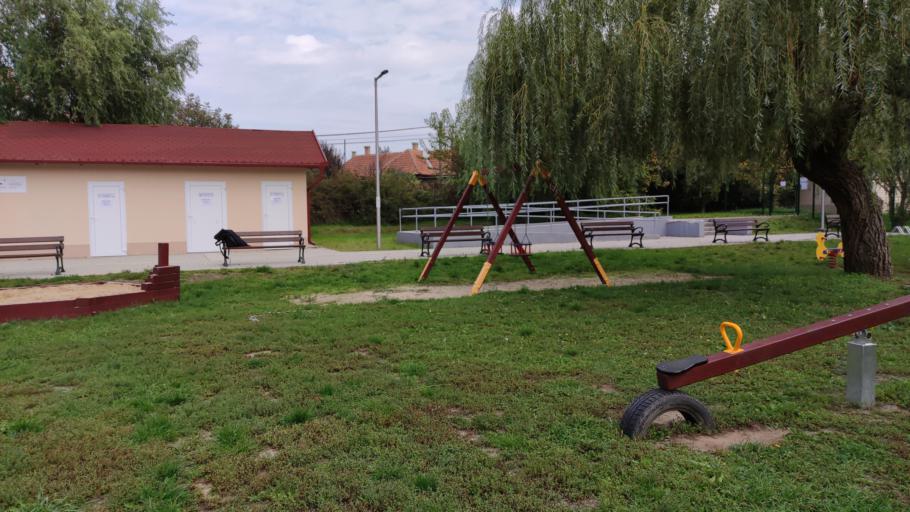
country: HU
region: Hajdu-Bihar
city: Hajduboszormeny
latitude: 47.6836
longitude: 21.5011
